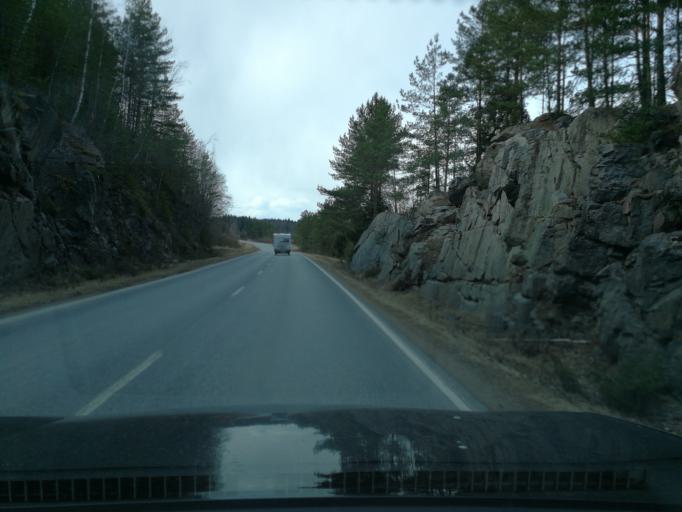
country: FI
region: Varsinais-Suomi
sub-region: Salo
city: Kisko
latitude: 60.2424
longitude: 23.5457
